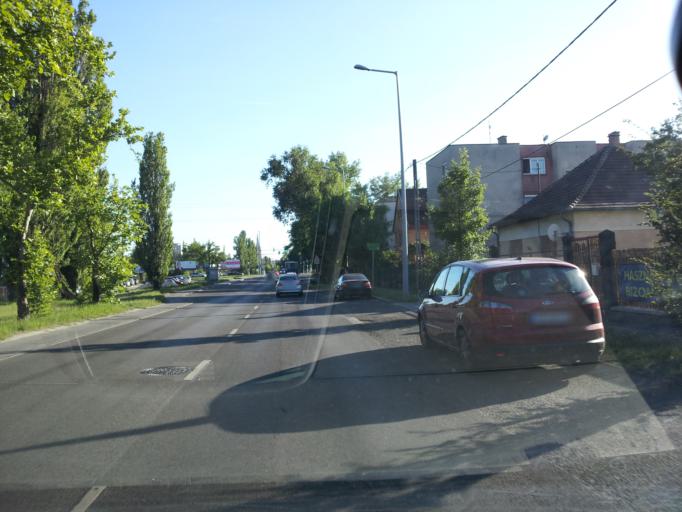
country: HU
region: Budapest
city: Budapest XIV. keruelet
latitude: 47.5252
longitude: 19.1194
